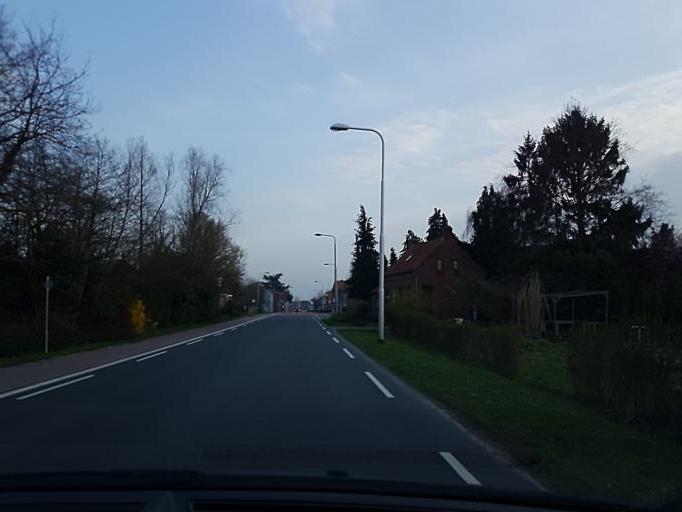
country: NL
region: Zeeland
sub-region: Gemeente Hulst
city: Hulst
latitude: 51.3430
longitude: 4.0338
